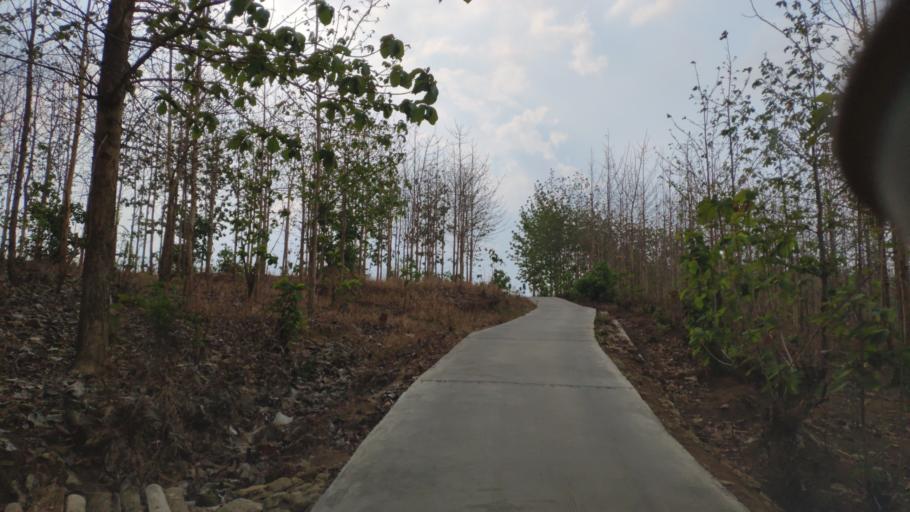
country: ID
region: Central Java
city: Gaplokan
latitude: -6.9090
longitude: 111.2542
